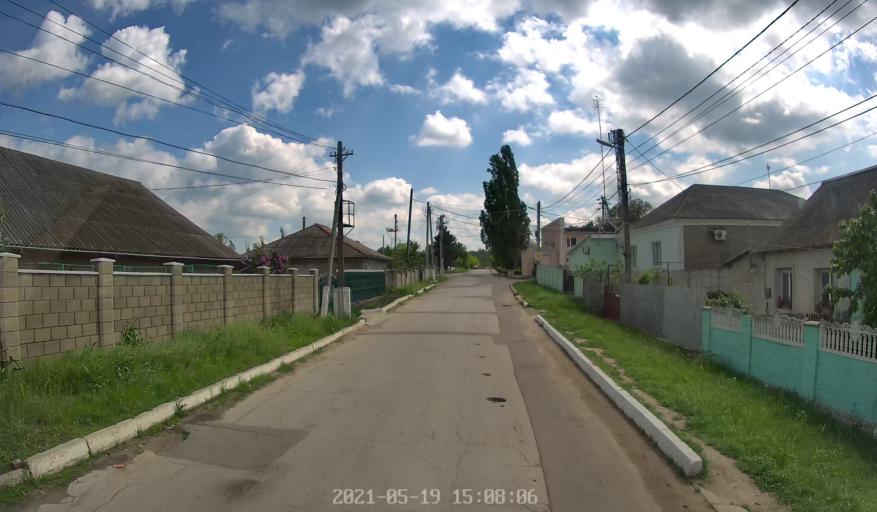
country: MD
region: Chisinau
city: Stauceni
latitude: 47.0618
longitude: 28.9483
